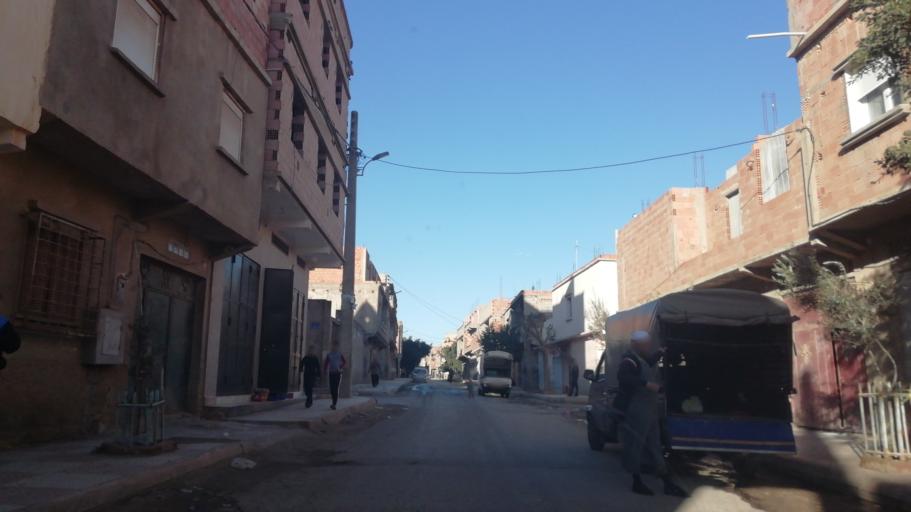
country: DZ
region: Oran
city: Sidi ech Chahmi
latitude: 35.6910
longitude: -0.4952
